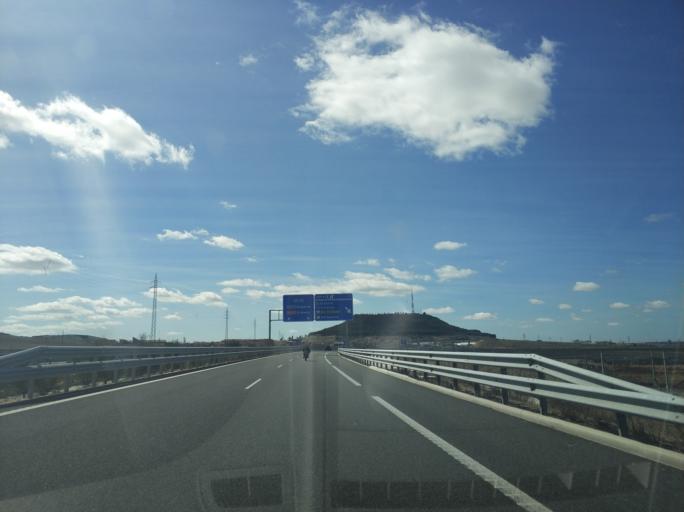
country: ES
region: Castille and Leon
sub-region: Provincia de Valladolid
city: Cisterniga
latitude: 41.6275
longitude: -4.6848
